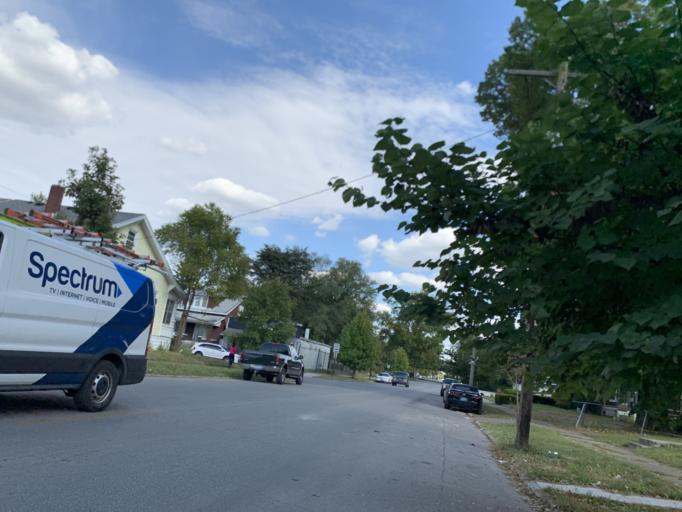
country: US
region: Indiana
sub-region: Floyd County
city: New Albany
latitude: 38.2462
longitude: -85.8135
